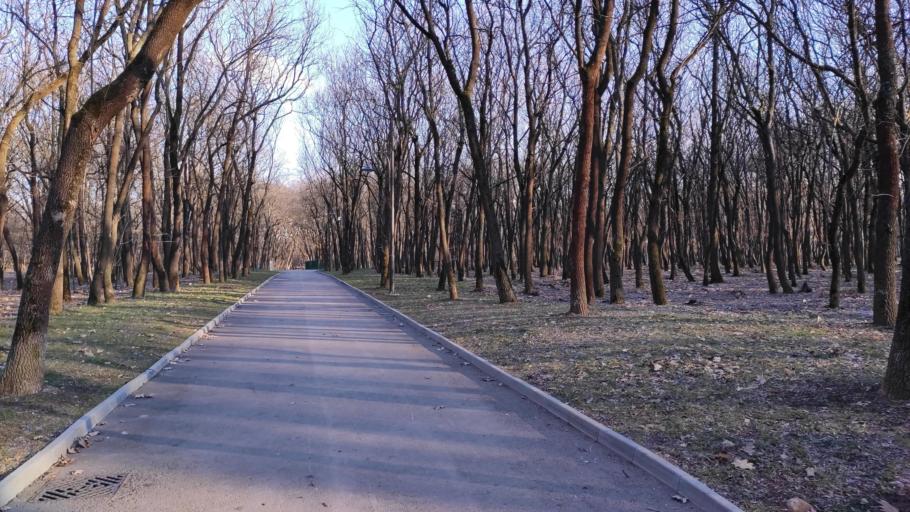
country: BG
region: Sofia-Capital
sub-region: Stolichna Obshtina
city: Sofia
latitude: 42.7112
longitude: 23.2781
